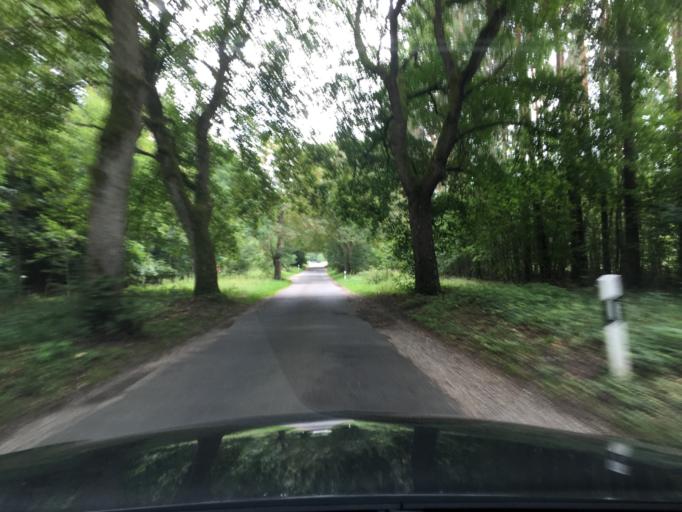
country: DE
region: Mecklenburg-Vorpommern
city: Waren
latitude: 53.4736
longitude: 12.7809
